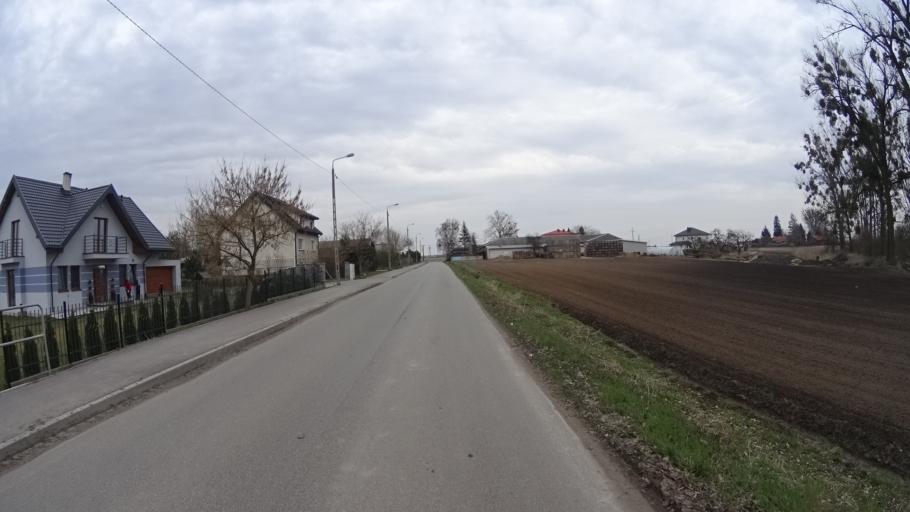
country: PL
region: Masovian Voivodeship
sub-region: Powiat warszawski zachodni
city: Blonie
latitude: 52.2162
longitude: 20.6502
